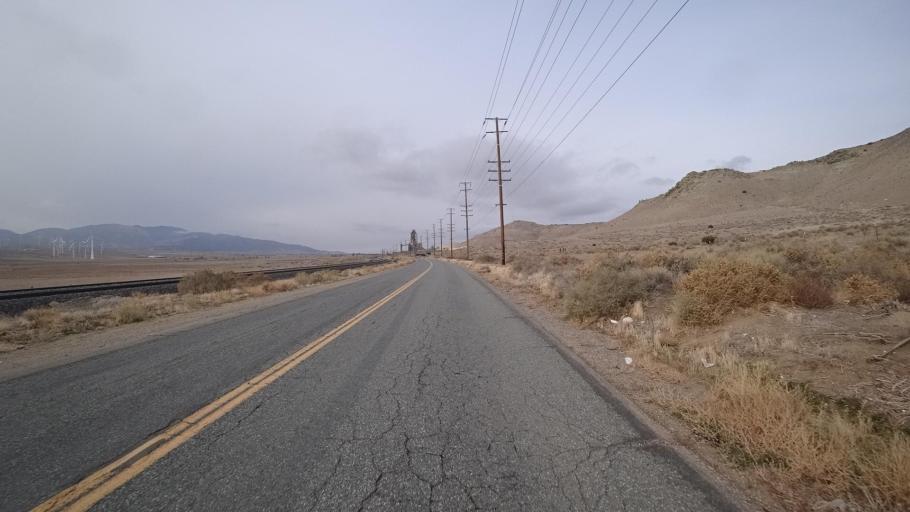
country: US
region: California
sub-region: Kern County
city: Tehachapi
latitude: 35.1214
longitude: -118.3494
